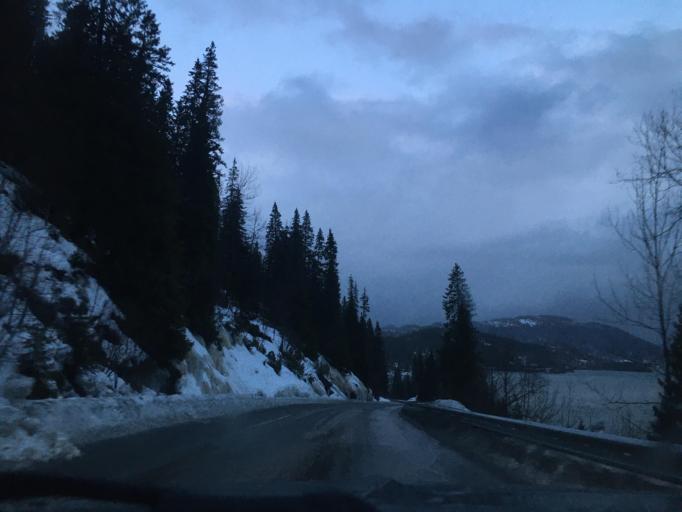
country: NO
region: Nordland
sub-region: Rana
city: Hauknes
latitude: 66.2985
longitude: 13.9257
